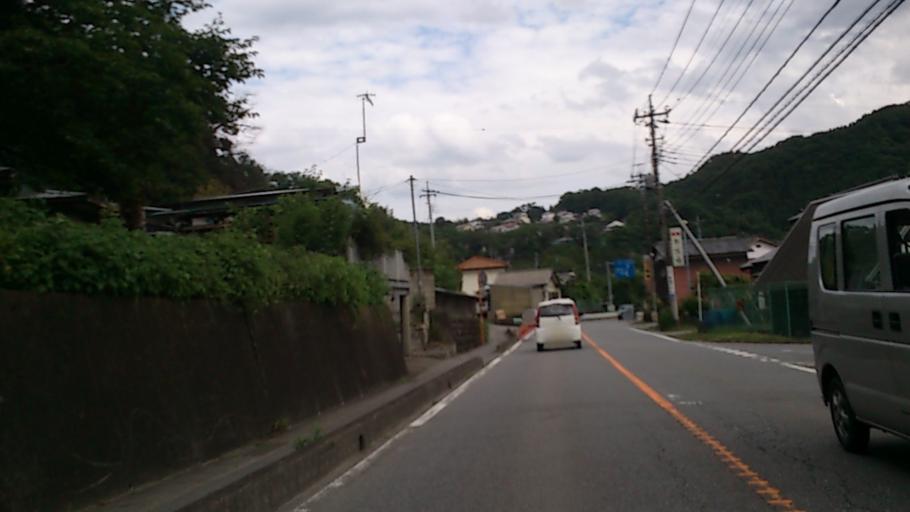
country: JP
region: Gunma
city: Tomioka
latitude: 36.2182
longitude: 138.8019
